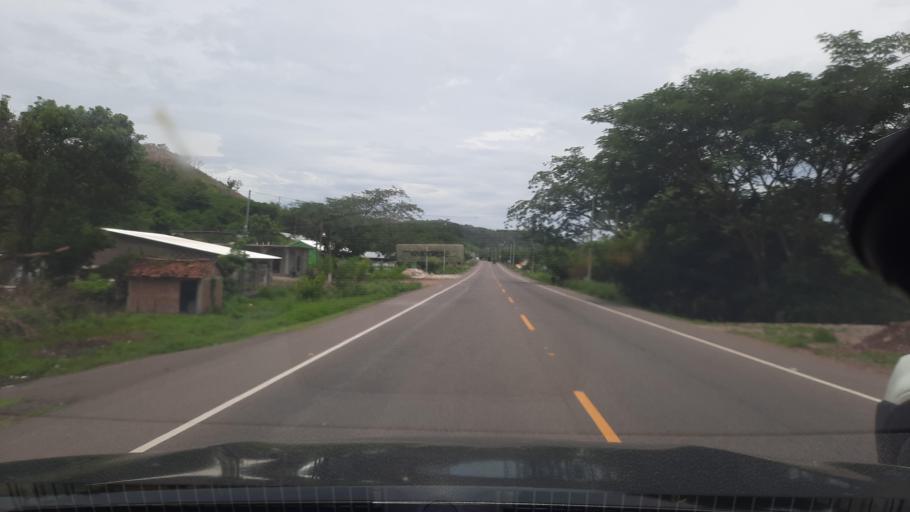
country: HN
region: Valle
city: Langue
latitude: 13.5849
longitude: -87.6905
